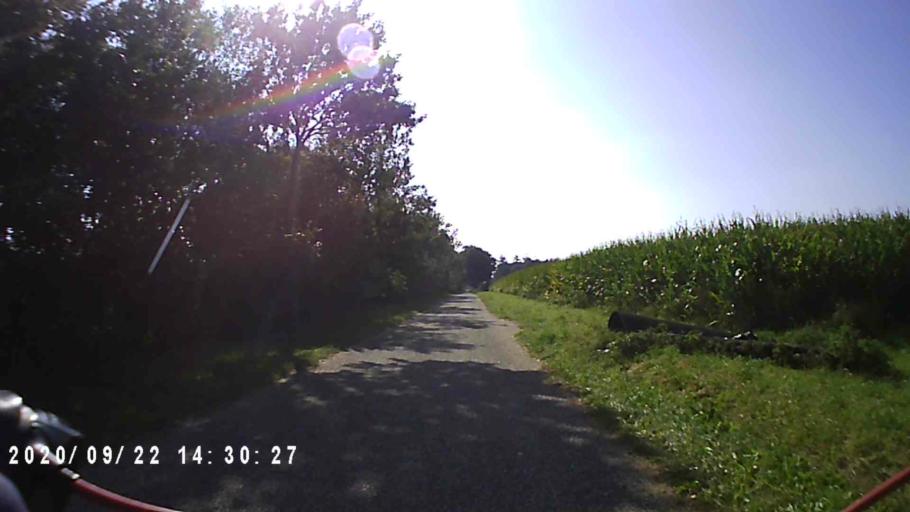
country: NL
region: Groningen
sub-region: Gemeente Leek
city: Leek
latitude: 53.0401
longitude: 6.3760
